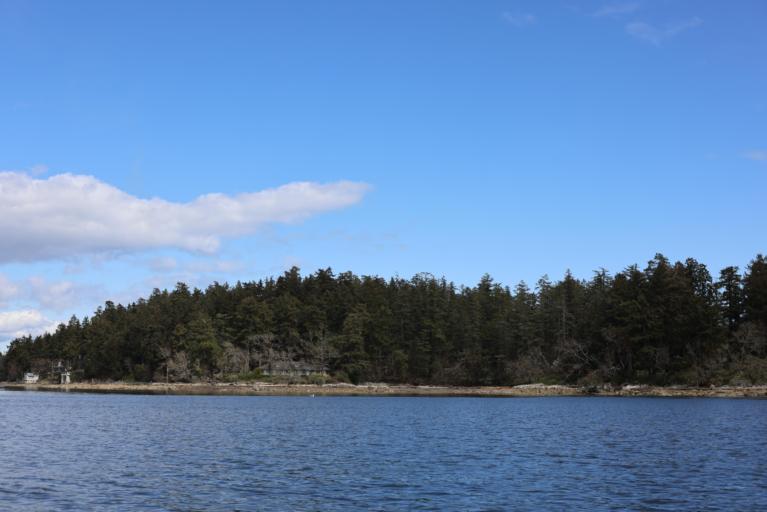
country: CA
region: British Columbia
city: North Saanich
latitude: 48.6251
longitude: -123.4820
